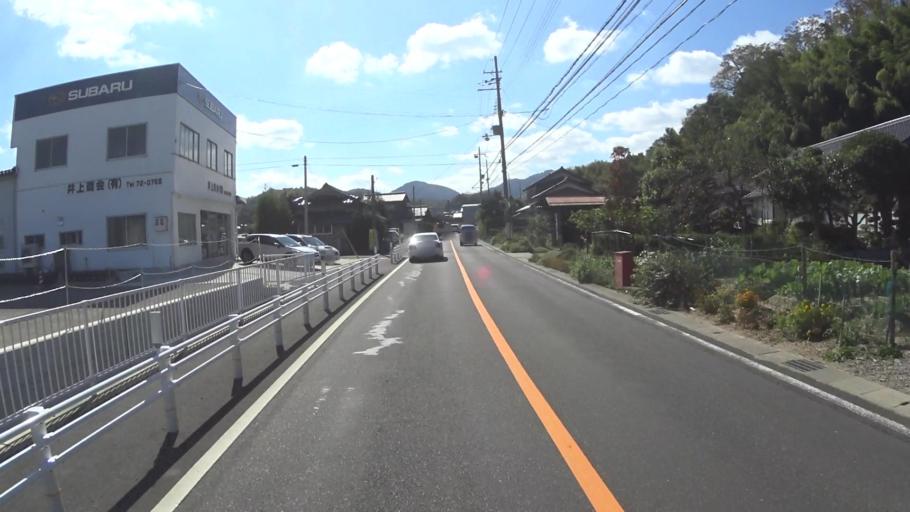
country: JP
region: Kyoto
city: Miyazu
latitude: 35.6560
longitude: 135.0326
